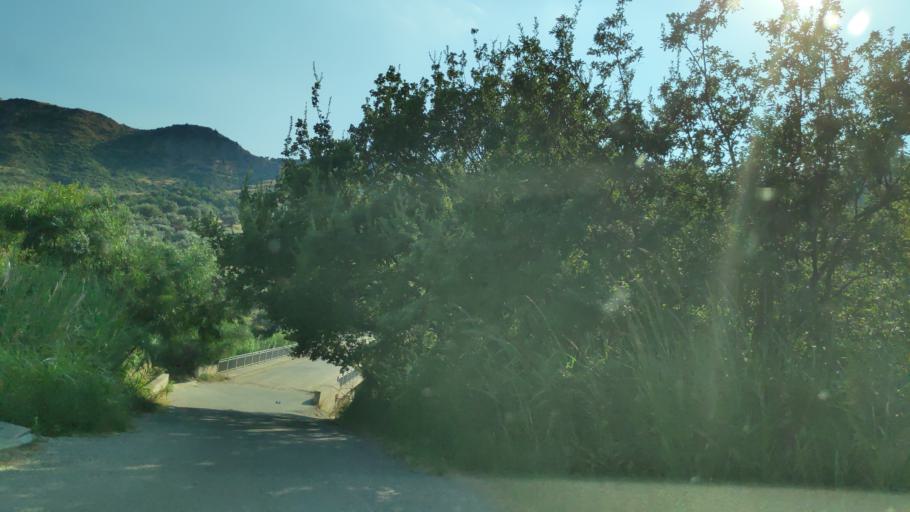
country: IT
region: Calabria
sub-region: Provincia di Reggio Calabria
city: Placanica
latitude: 38.4137
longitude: 16.4412
